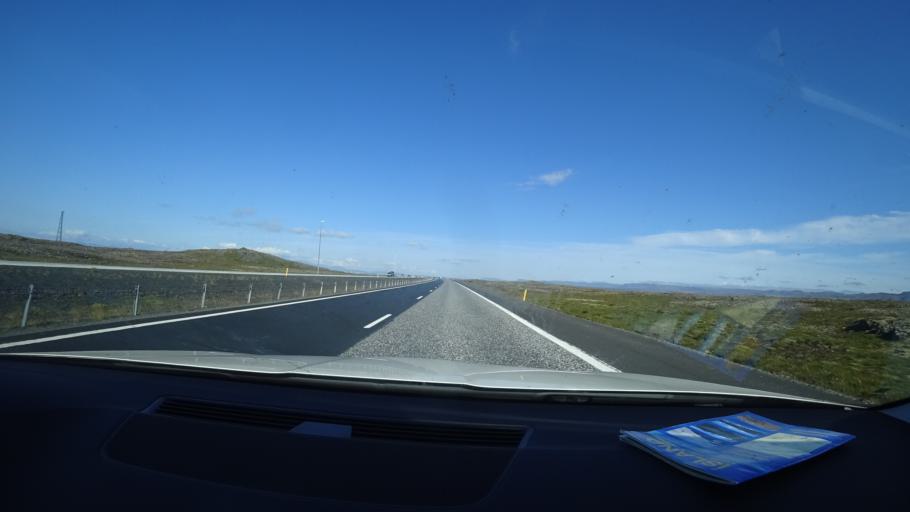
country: IS
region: Southern Peninsula
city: Vogar
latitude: 64.0006
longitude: -22.2380
